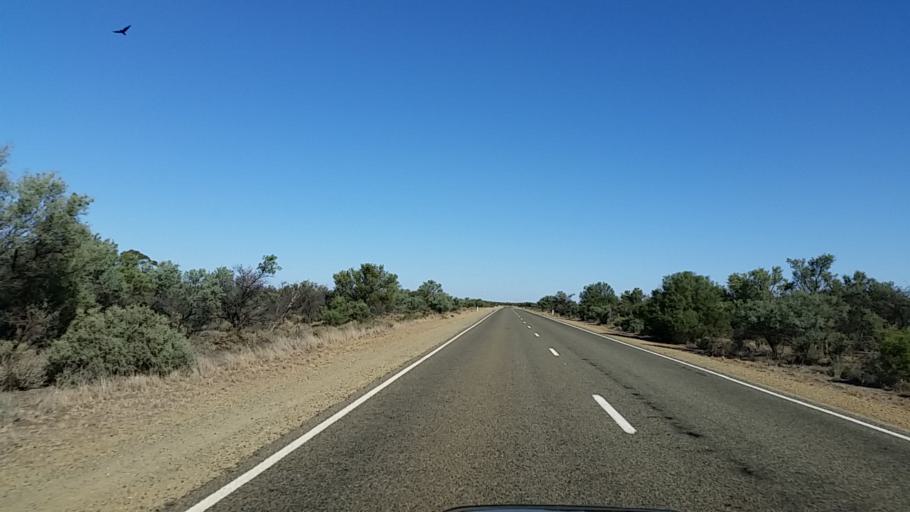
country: AU
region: South Australia
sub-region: Flinders Ranges
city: Quorn
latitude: -32.3810
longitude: 138.5010
